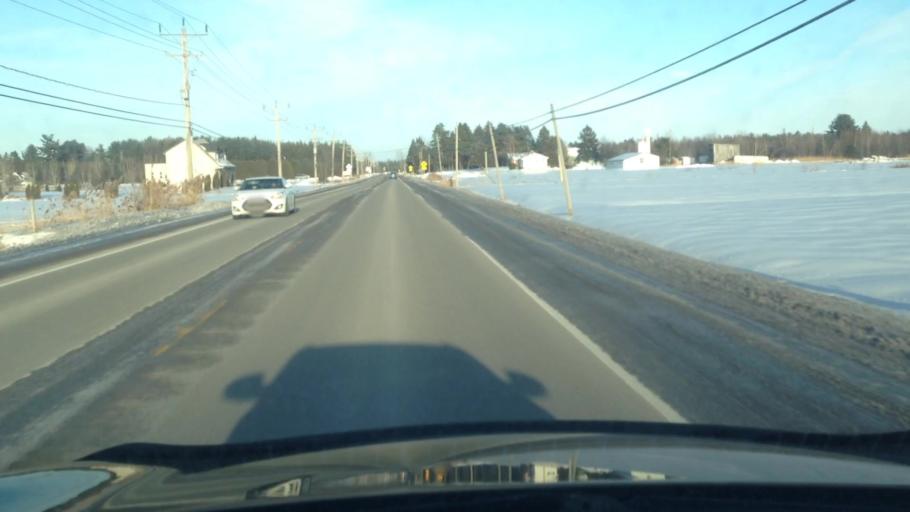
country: CA
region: Quebec
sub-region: Laurentides
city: Sainte-Sophie
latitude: 45.8031
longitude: -73.9320
